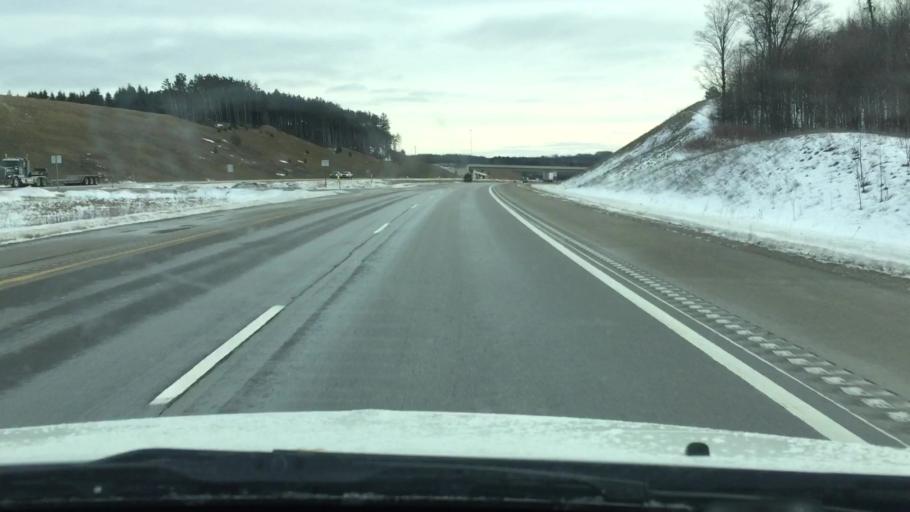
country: US
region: Michigan
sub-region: Wexford County
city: Manton
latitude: 44.4158
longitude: -85.3810
